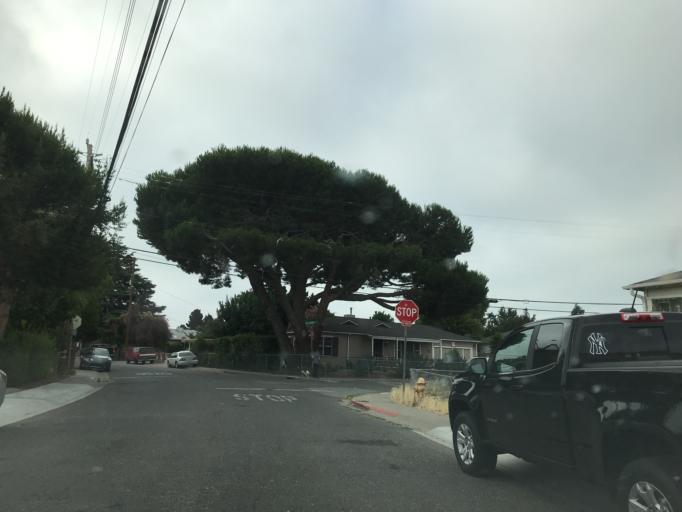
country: US
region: California
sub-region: San Mateo County
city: East Palo Alto
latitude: 37.4594
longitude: -122.1290
